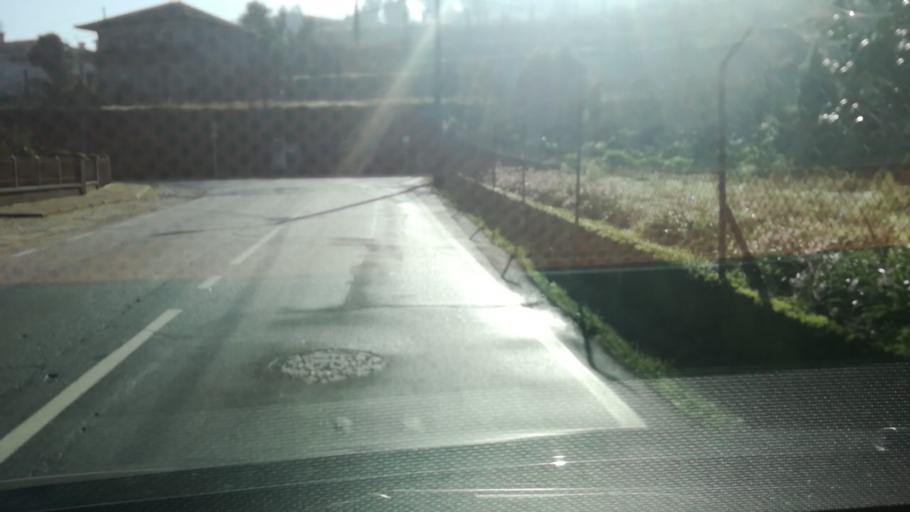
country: PT
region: Braga
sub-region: Guimaraes
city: Ponte
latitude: 41.5208
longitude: -8.3397
